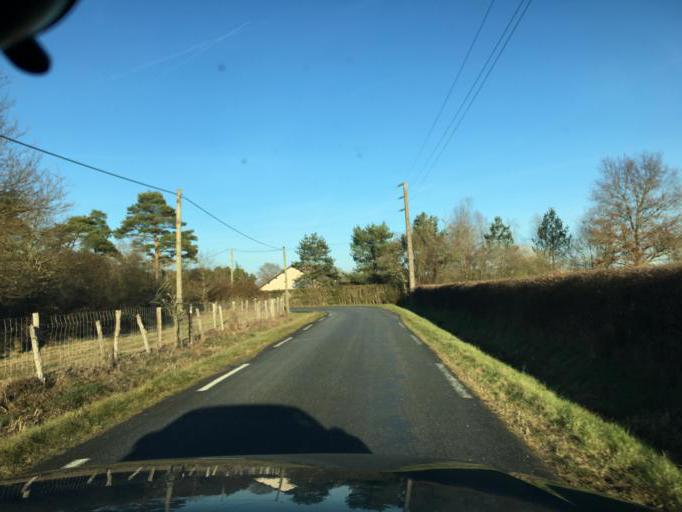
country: FR
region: Centre
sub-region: Departement du Loiret
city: Ligny-le-Ribault
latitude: 47.7081
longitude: 1.7714
